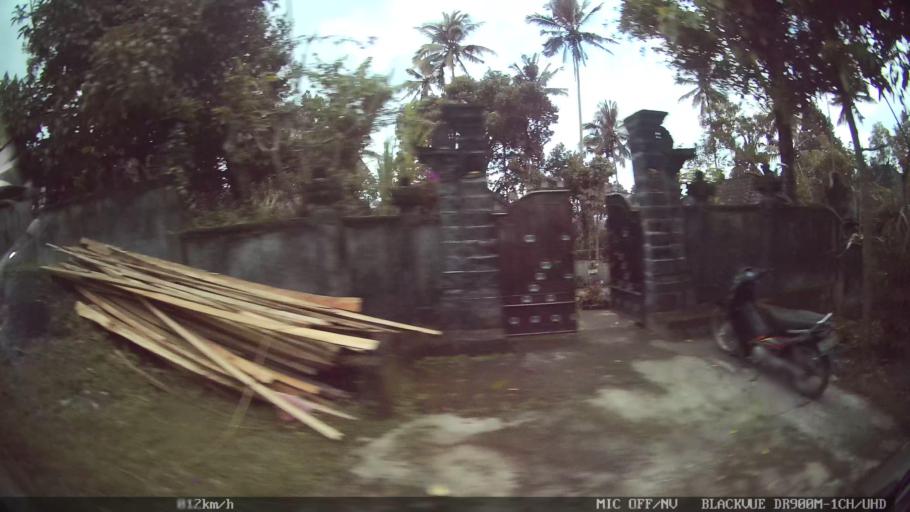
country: ID
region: Bali
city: Banjar Wangsian
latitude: -8.4500
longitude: 115.4221
